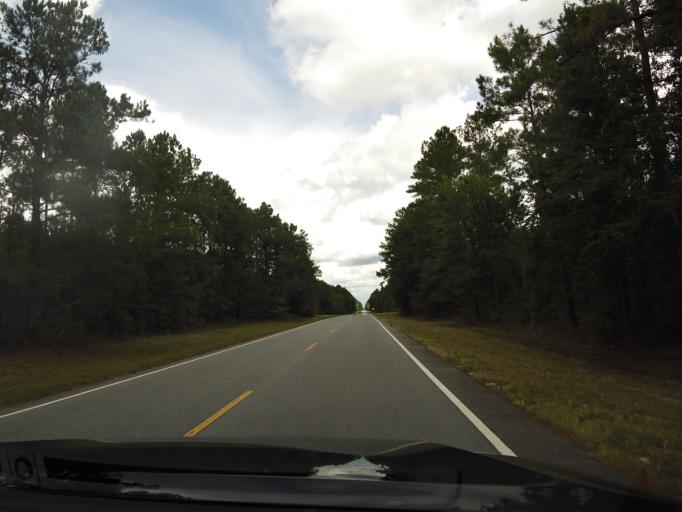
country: US
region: Georgia
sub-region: Brantley County
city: Nahunta
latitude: 31.0533
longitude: -82.0166
